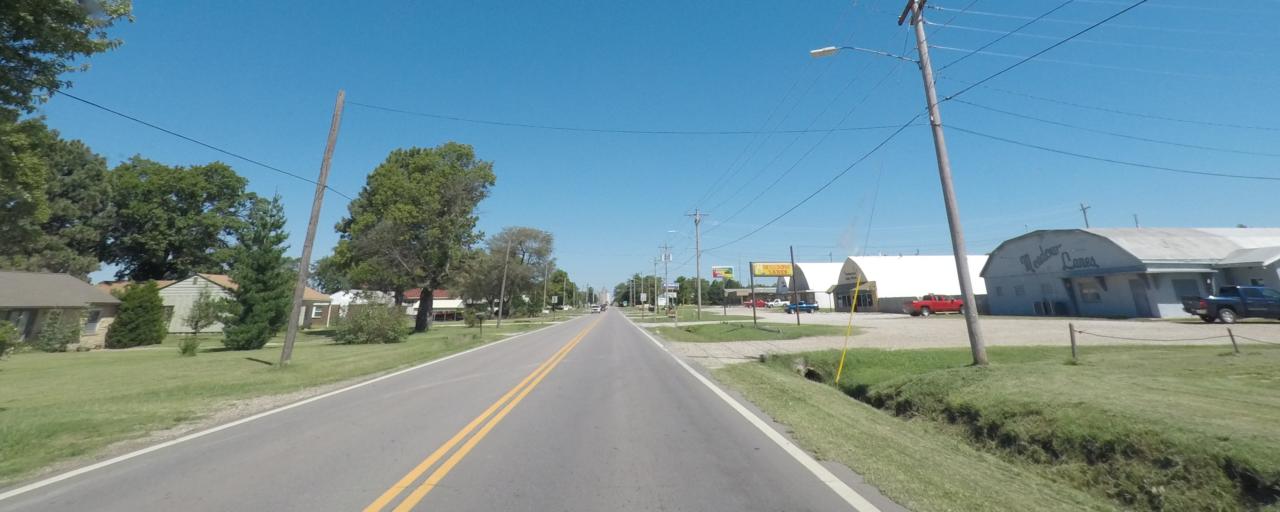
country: US
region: Kansas
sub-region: Sumner County
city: Wellington
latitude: 37.2864
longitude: -97.3943
